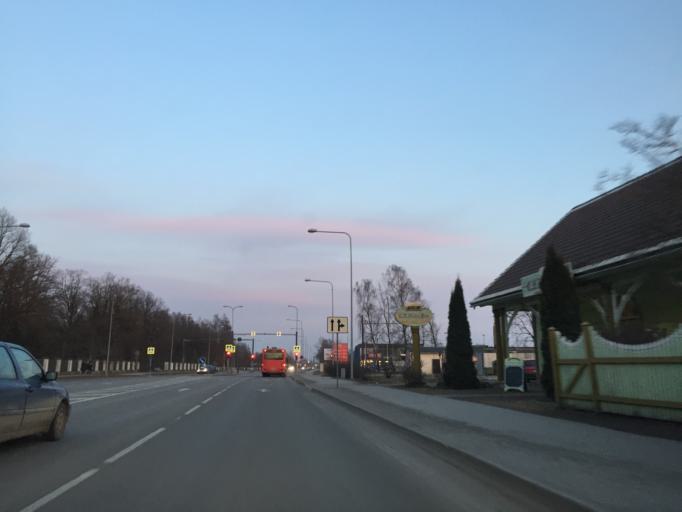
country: EE
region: Paernumaa
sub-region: Paernu linn
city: Parnu
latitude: 58.3766
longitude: 24.5341
